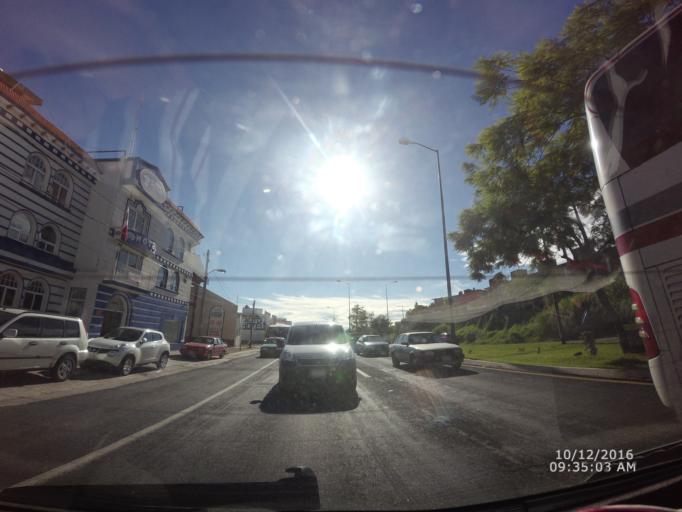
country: TR
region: Sivas
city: Karayun
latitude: 39.6692
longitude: 37.2968
